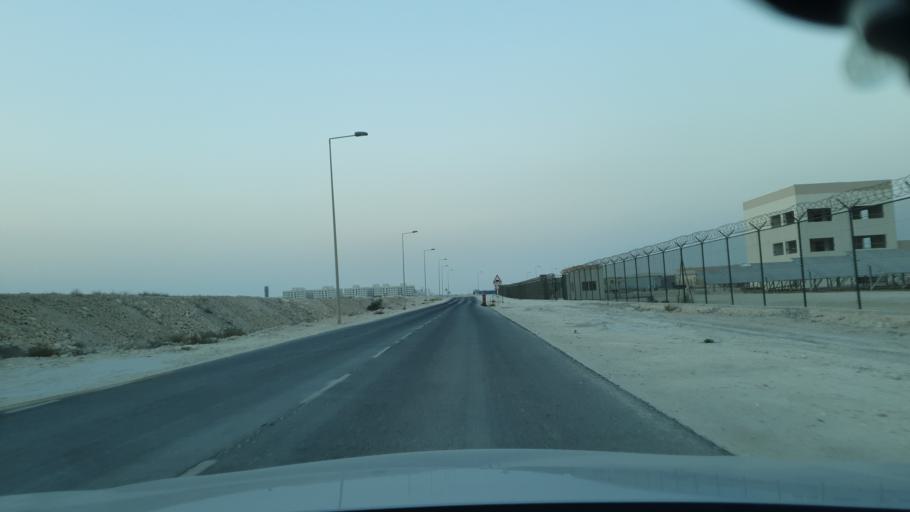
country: BH
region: Central Governorate
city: Dar Kulayb
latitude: 25.9733
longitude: 50.6096
